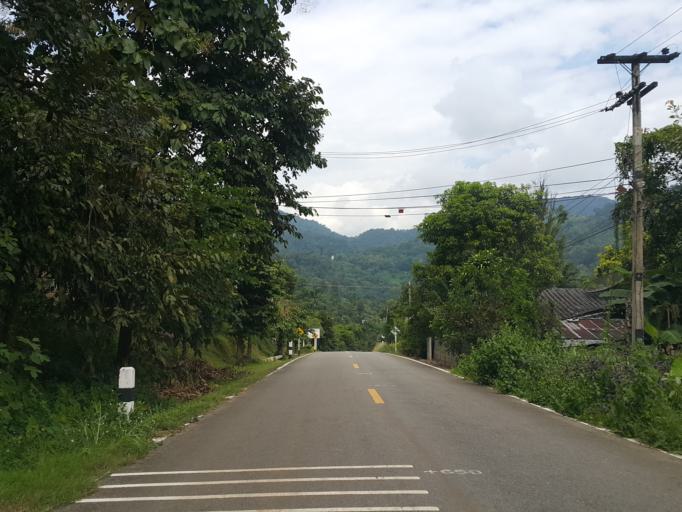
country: TH
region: Mae Hong Son
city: Mae Hong Son
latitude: 19.4783
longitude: 97.9645
